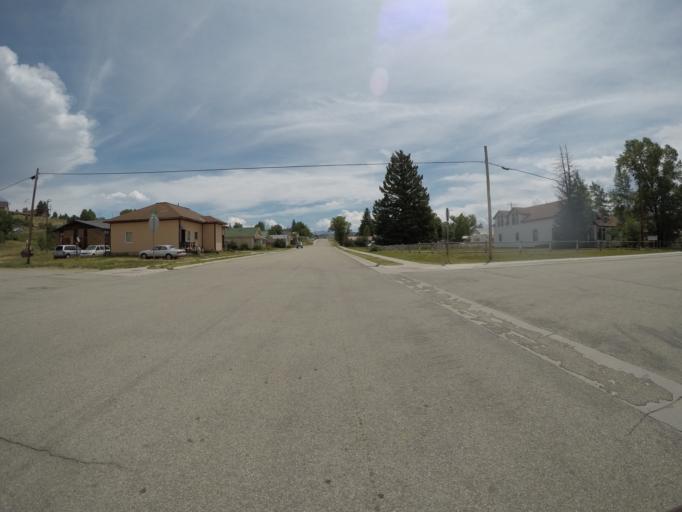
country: US
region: Colorado
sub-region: Grand County
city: Granby
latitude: 40.0862
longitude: -105.9373
